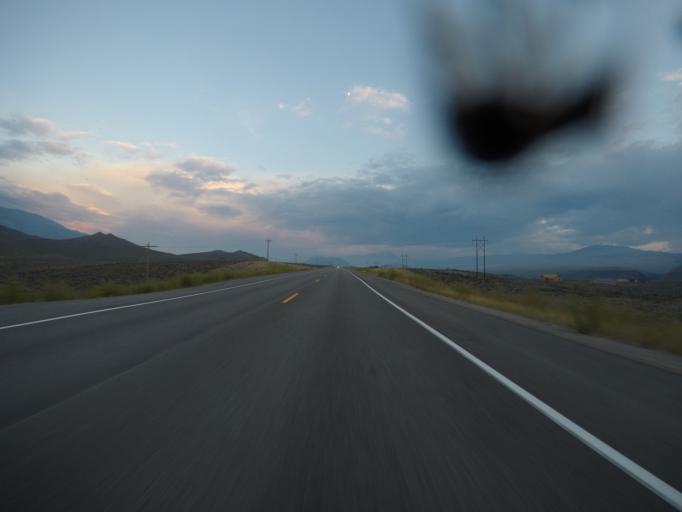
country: US
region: Colorado
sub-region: Grand County
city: Kremmling
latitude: 39.9563
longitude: -106.3480
